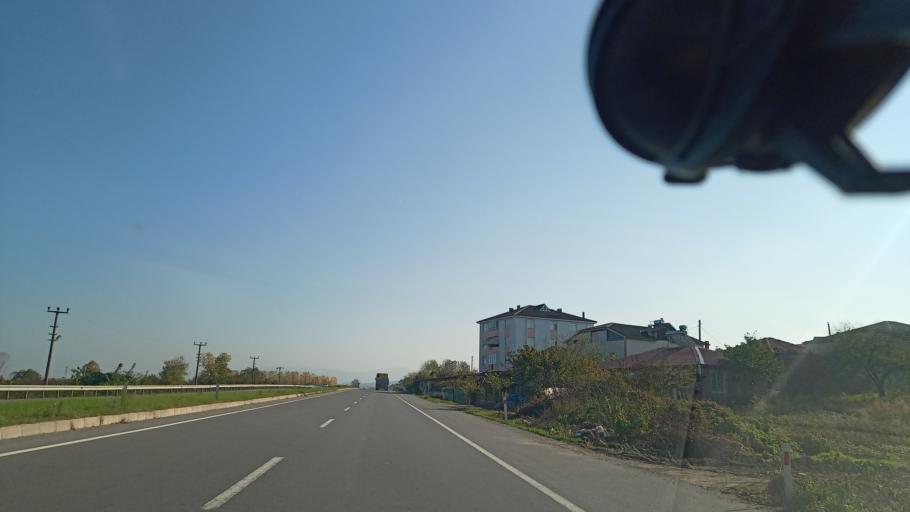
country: TR
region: Sakarya
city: Karasu
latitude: 41.0743
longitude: 30.7858
